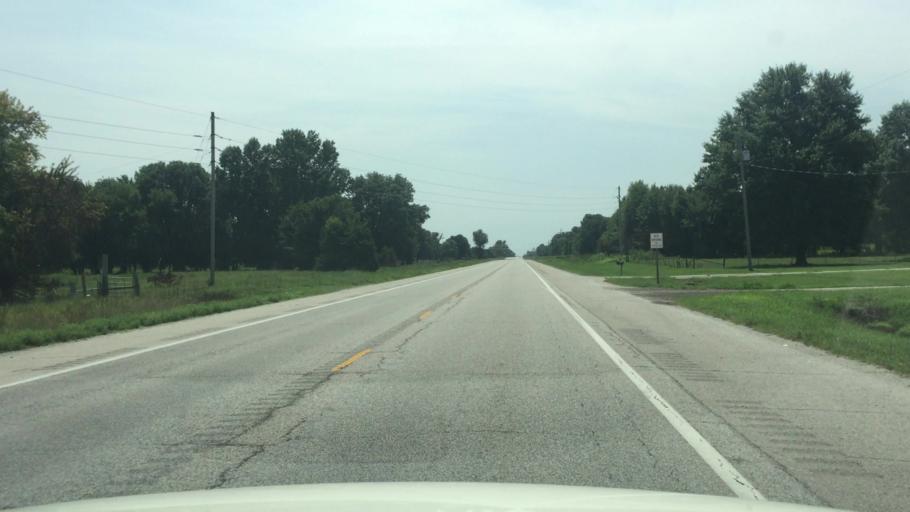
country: US
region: Kansas
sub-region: Cherokee County
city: Galena
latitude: 37.1280
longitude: -94.7044
